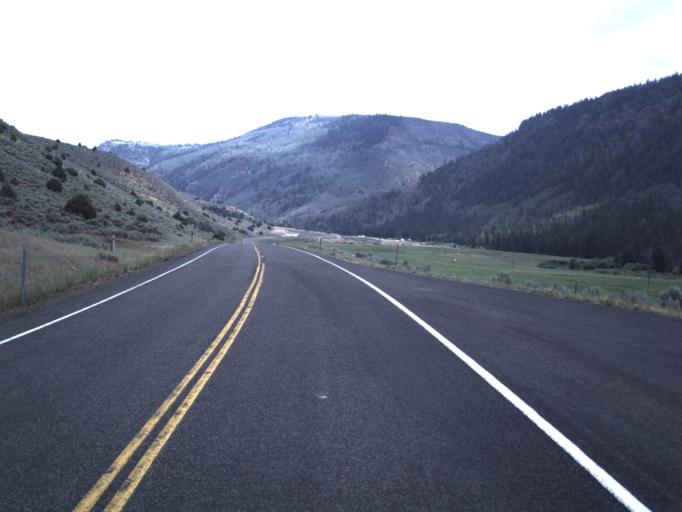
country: US
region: Utah
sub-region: Summit County
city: Francis
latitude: 40.4532
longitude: -110.8821
